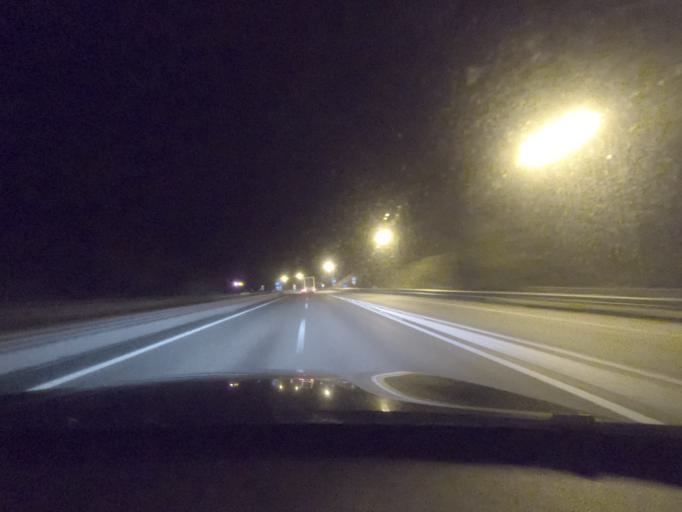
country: PT
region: Porto
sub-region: Amarante
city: Amarante
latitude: 41.2551
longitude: -8.0407
